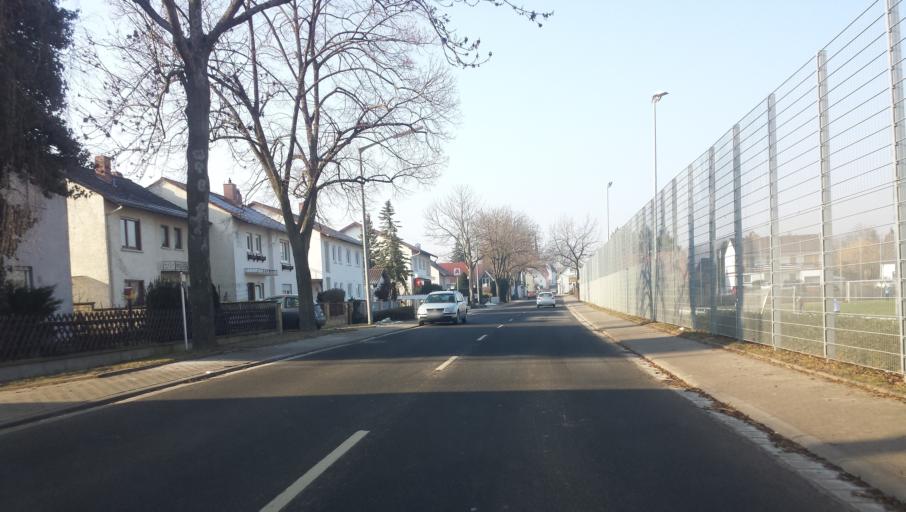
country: DE
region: Rheinland-Pfalz
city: Monsheim
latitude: 49.6346
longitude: 8.2163
